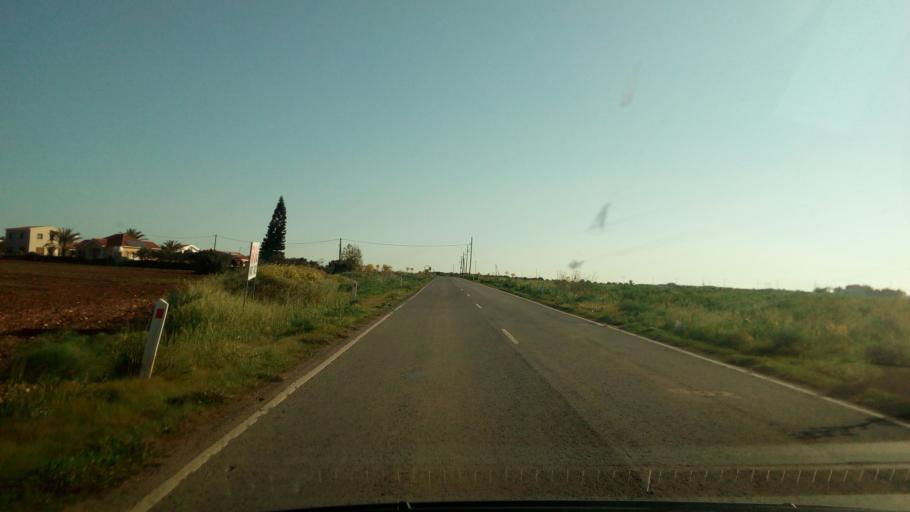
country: CY
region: Larnaka
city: Kofinou
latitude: 34.7807
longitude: 33.4712
